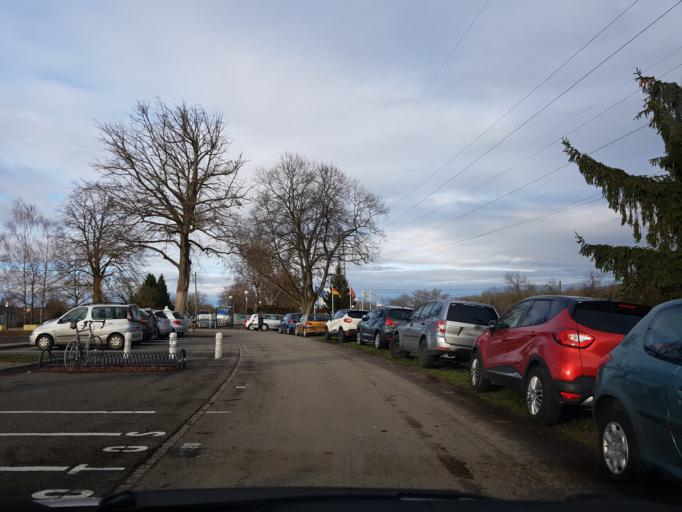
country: FR
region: Alsace
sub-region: Departement du Haut-Rhin
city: Kembs
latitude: 47.6860
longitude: 7.5076
